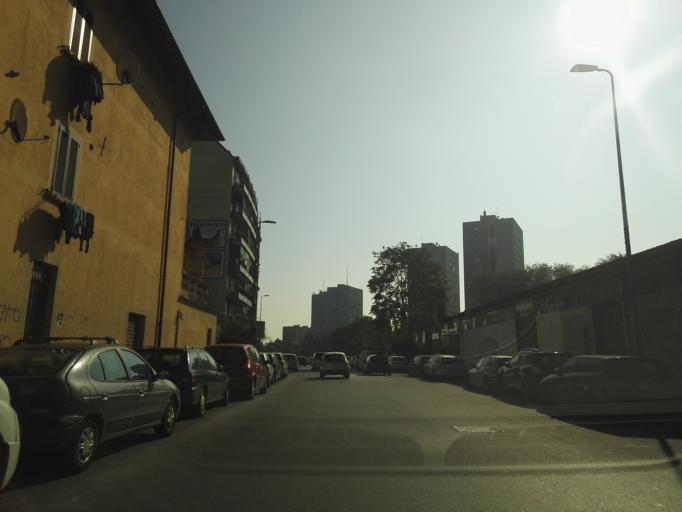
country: IT
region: Lombardy
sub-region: Citta metropolitana di Milano
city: Chiaravalle
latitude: 45.4364
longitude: 9.2172
